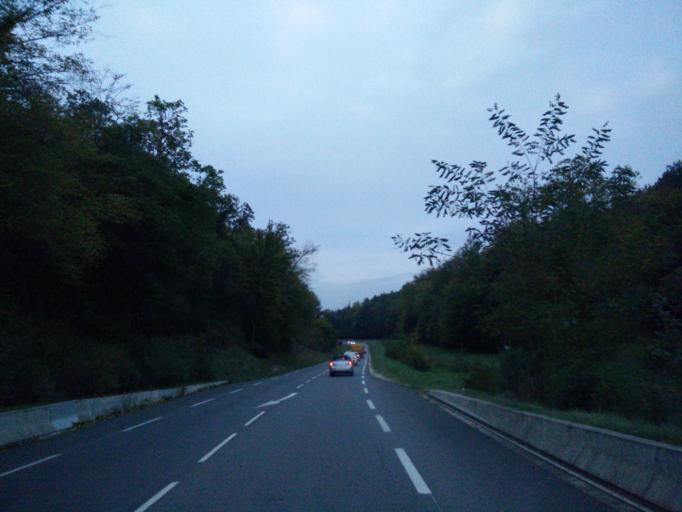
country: FR
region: Aquitaine
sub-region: Departement de la Dordogne
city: Sarlat-la-Caneda
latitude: 44.8916
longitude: 1.2002
